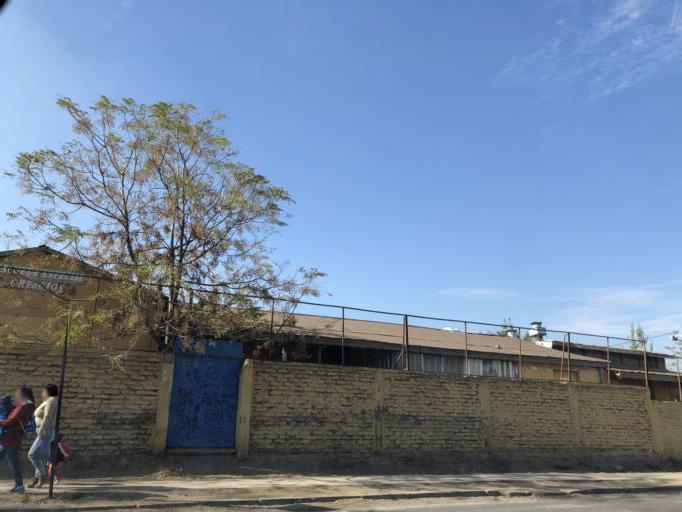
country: CL
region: Santiago Metropolitan
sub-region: Provincia de Cordillera
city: Puente Alto
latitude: -33.6168
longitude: -70.5720
